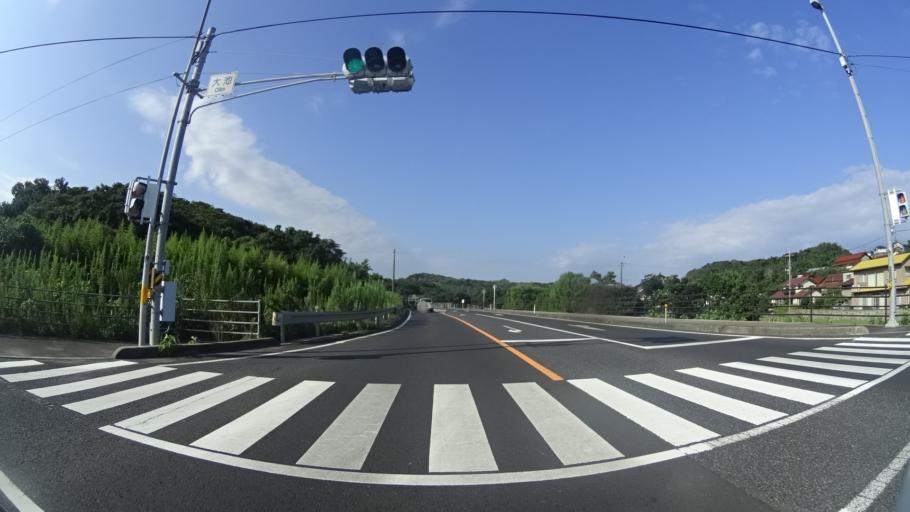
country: JP
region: Shimane
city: Izumo
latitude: 35.3170
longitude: 132.6634
